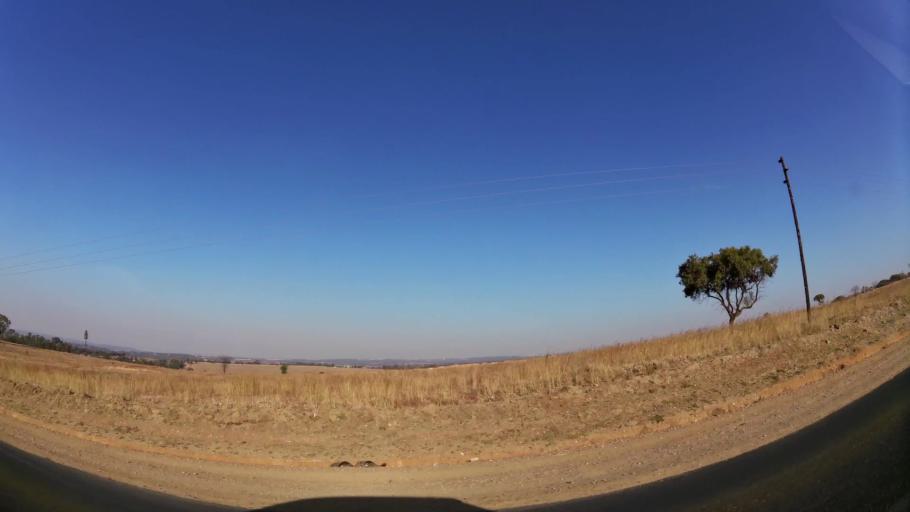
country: ZA
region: Gauteng
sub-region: City of Johannesburg Metropolitan Municipality
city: Diepsloot
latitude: -25.9896
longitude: 27.9339
